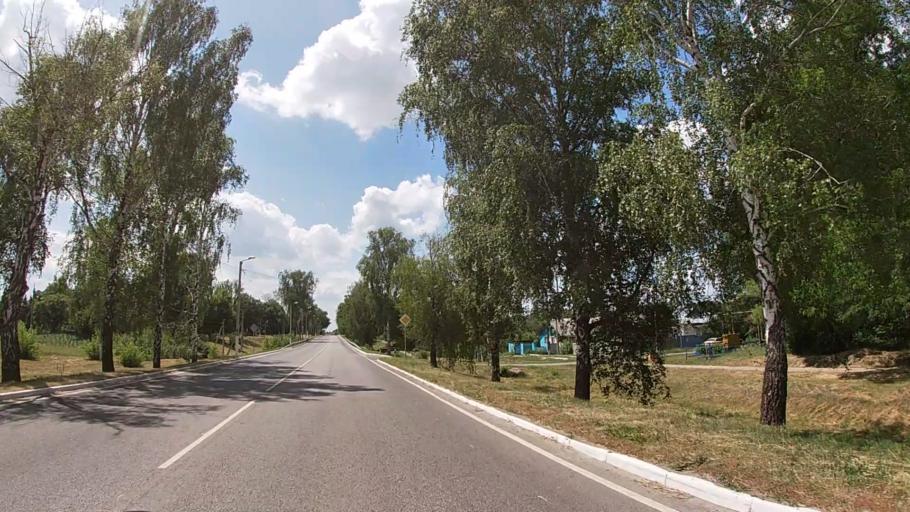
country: RU
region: Belgorod
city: Grayvoron
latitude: 50.4883
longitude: 35.6927
